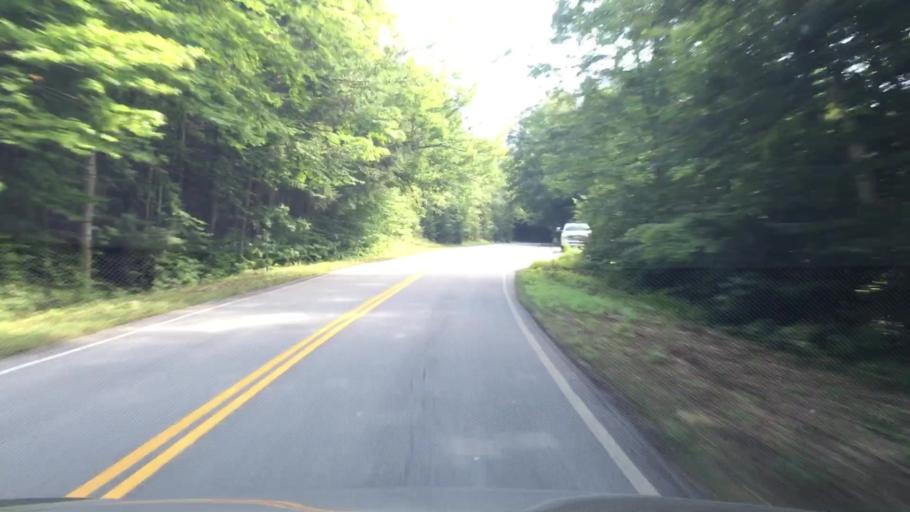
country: US
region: New Hampshire
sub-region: Carroll County
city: North Conway
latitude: 44.0482
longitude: -71.2763
